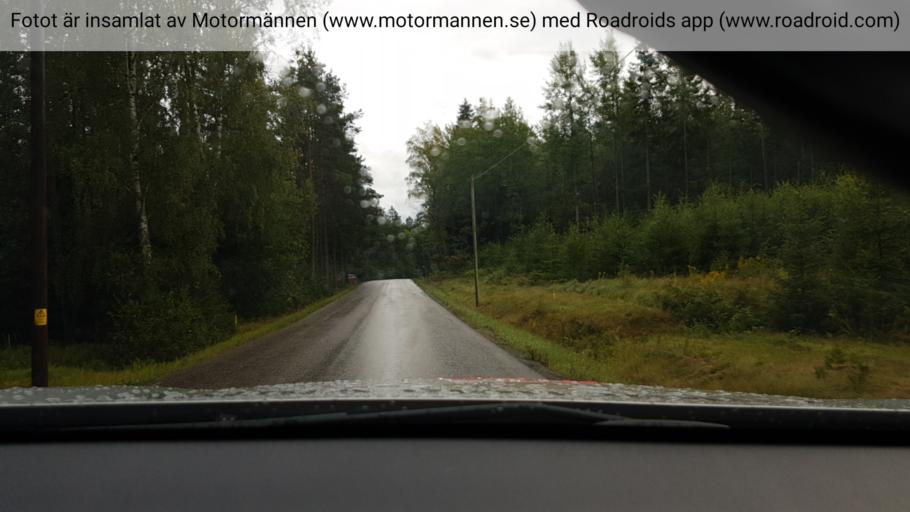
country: SE
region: Stockholm
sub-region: Haninge Kommun
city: Jordbro
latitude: 59.0814
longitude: 18.0518
